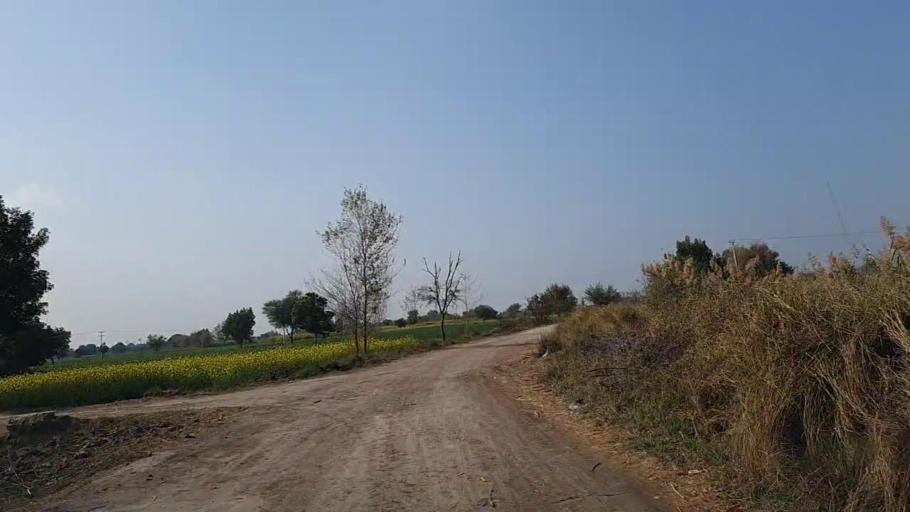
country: PK
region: Sindh
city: Jam Sahib
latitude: 26.2886
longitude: 68.5655
